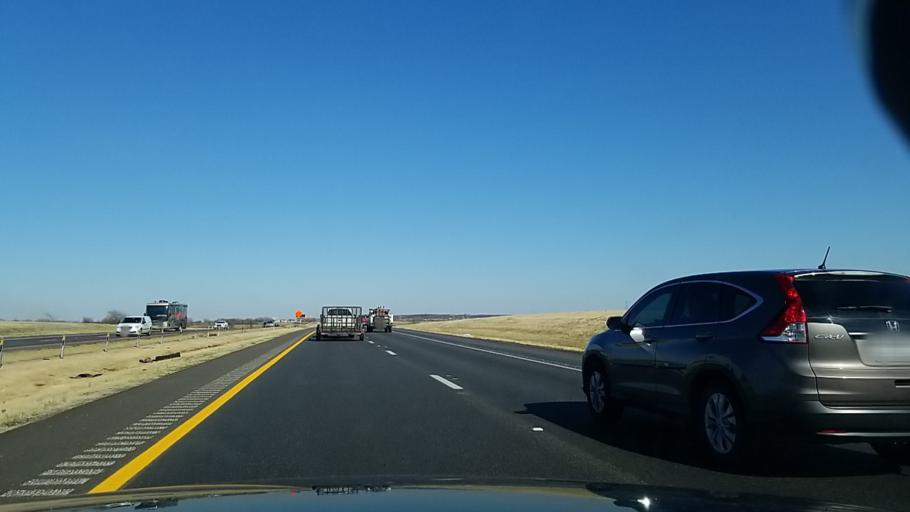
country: US
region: Texas
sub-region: Denton County
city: Northlake
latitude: 33.0848
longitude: -97.2328
